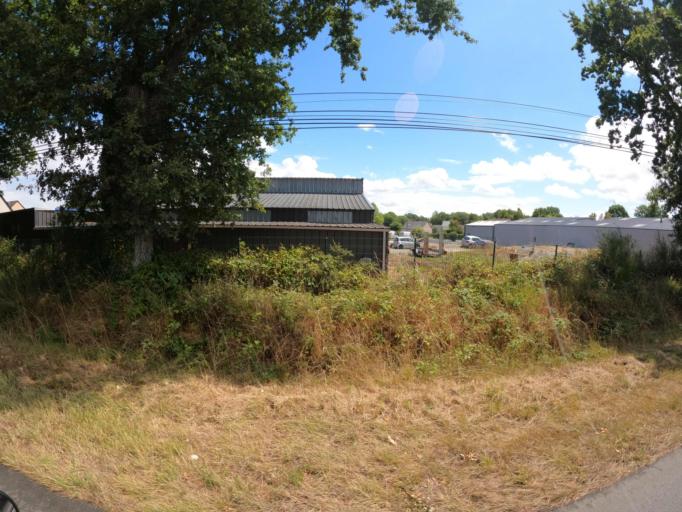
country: FR
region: Pays de la Loire
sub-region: Departement de Maine-et-Loire
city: Feneu
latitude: 47.5780
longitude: -0.5923
